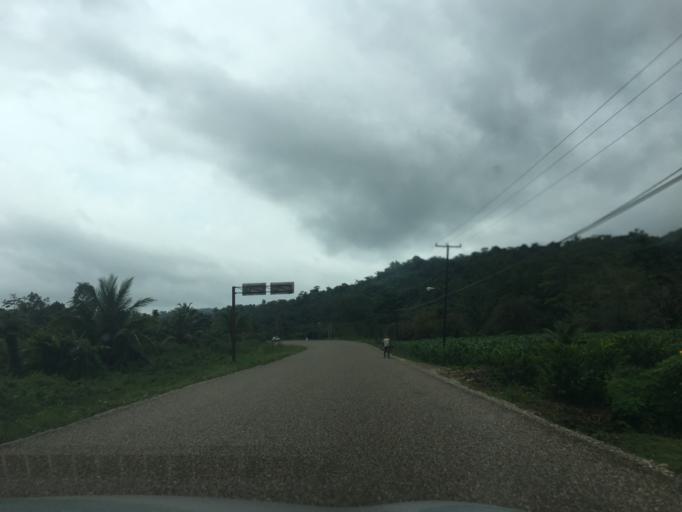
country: BZ
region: Stann Creek
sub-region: Dangriga
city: Dangriga
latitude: 17.0463
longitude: -88.5319
